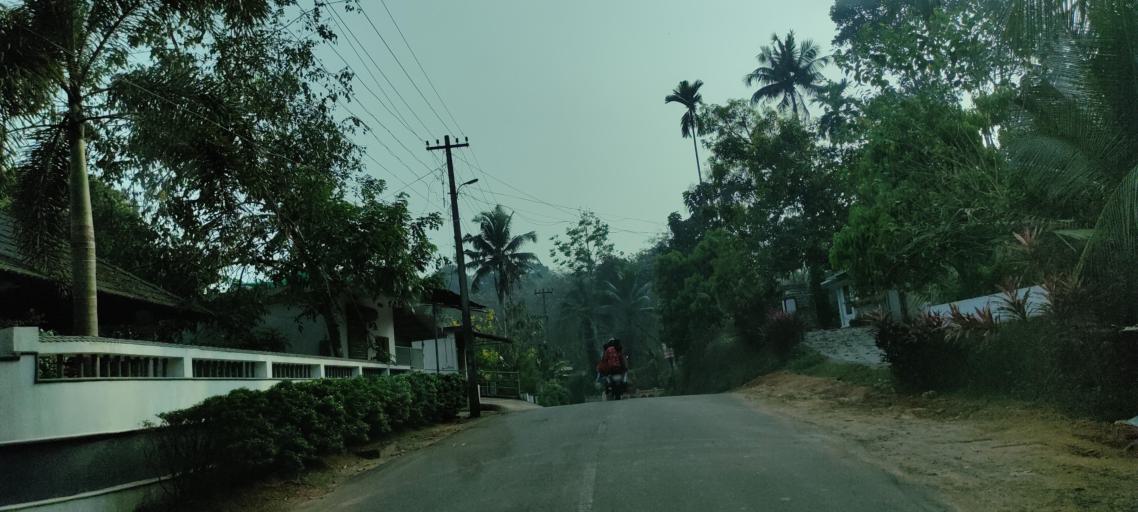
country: IN
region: Kerala
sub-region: Ernakulam
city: Piravam
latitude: 9.7868
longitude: 76.4978
